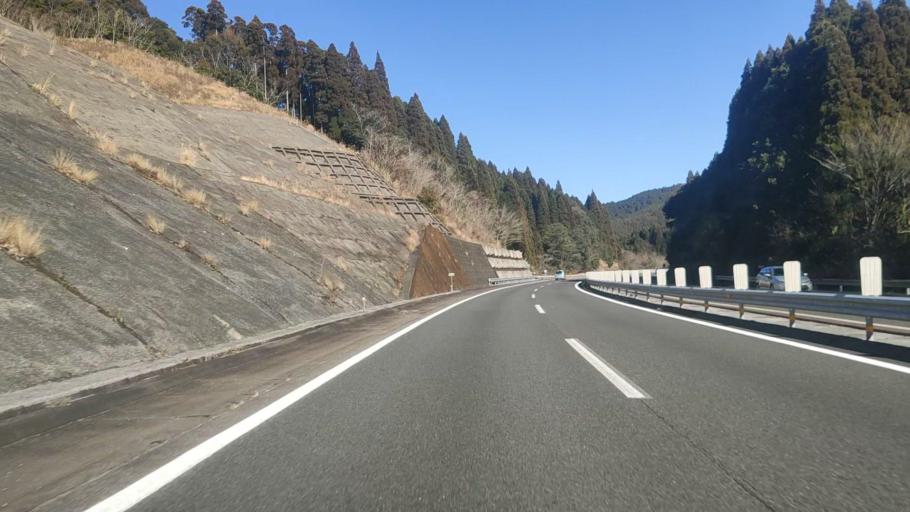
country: JP
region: Miyazaki
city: Miyakonojo
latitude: 31.8214
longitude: 131.2192
